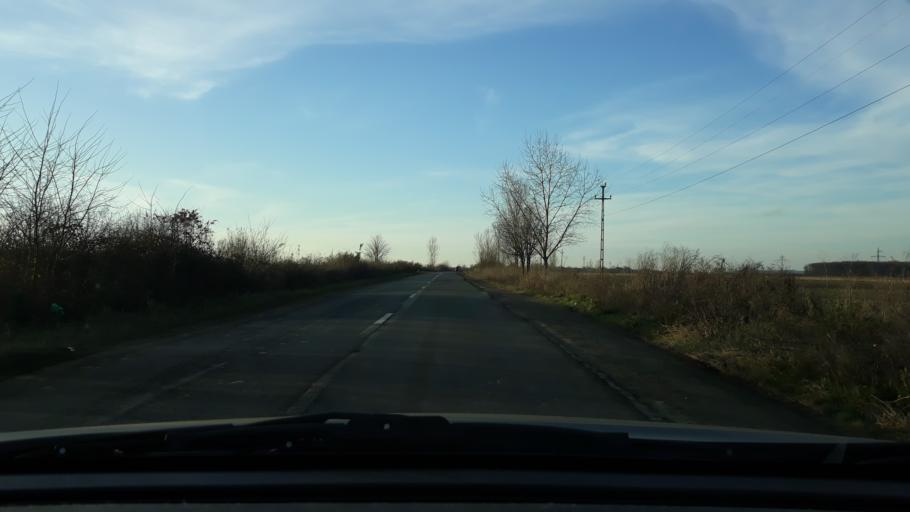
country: RO
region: Bihor
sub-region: Comuna Suplacu de Barcau
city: Suplacu de Barcau
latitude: 47.2664
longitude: 22.5048
